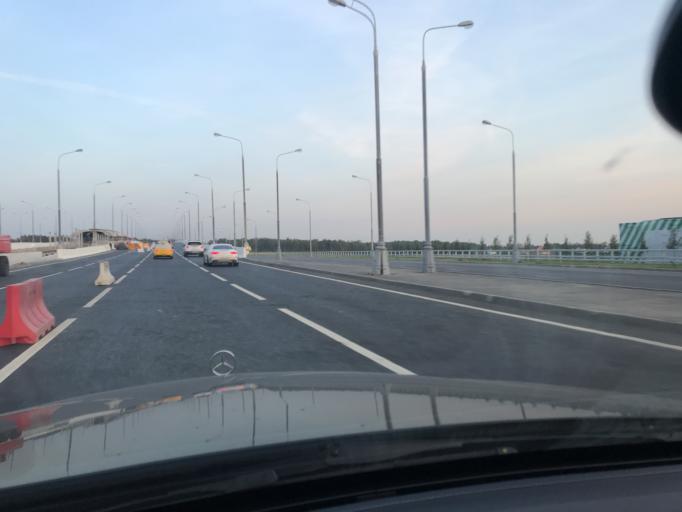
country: RU
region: Moskovskaya
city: Mosrentgen
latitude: 55.5858
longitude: 37.4343
